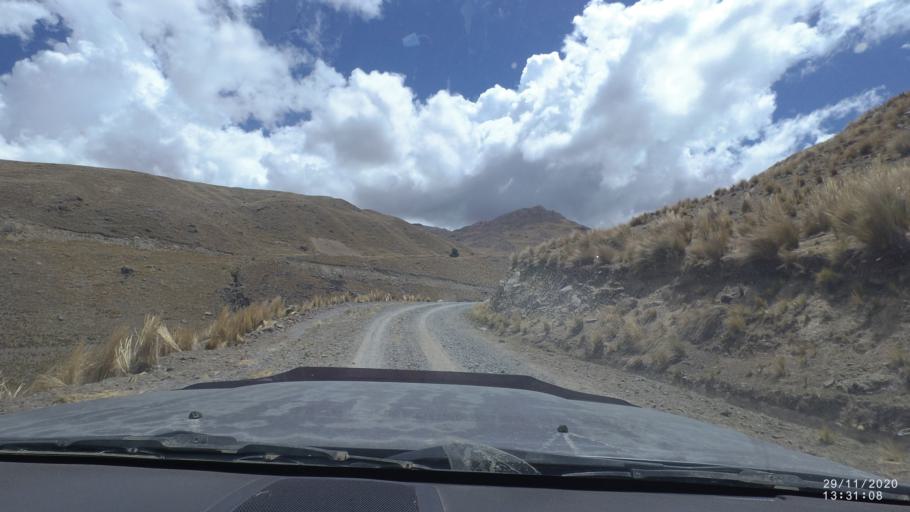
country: BO
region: Cochabamba
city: Cochabamba
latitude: -17.1041
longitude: -66.3426
